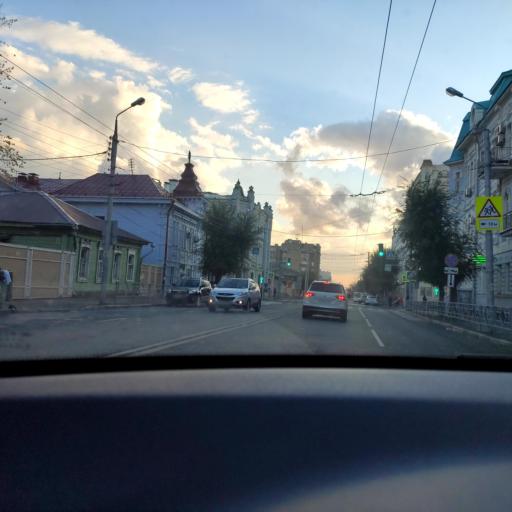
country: RU
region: Samara
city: Samara
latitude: 53.1950
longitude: 50.1067
